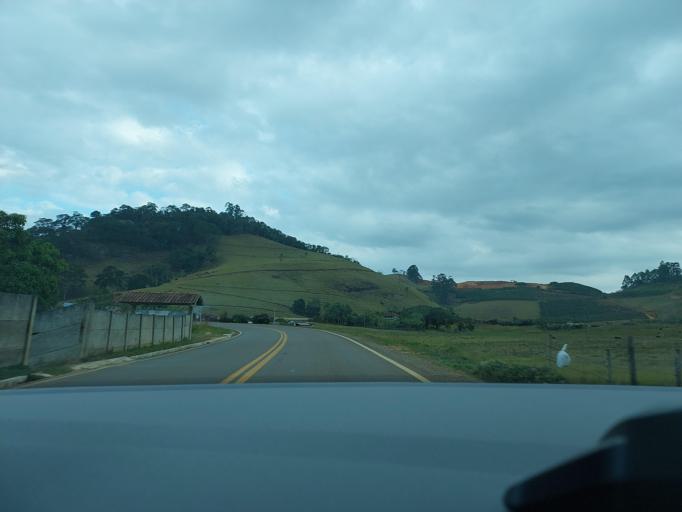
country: BR
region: Minas Gerais
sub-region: Mirai
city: Mirai
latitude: -21.0065
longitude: -42.5533
